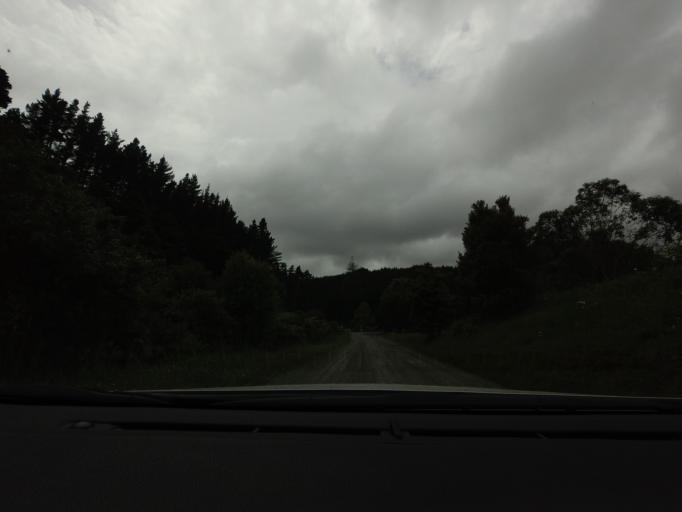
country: NZ
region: Auckland
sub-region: Auckland
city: Warkworth
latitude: -36.5008
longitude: 174.6266
